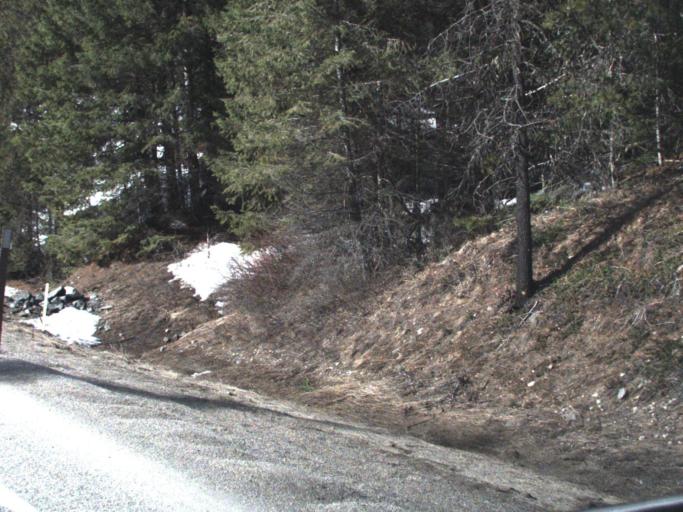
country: US
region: Washington
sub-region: Stevens County
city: Chewelah
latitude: 48.5678
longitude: -117.5553
